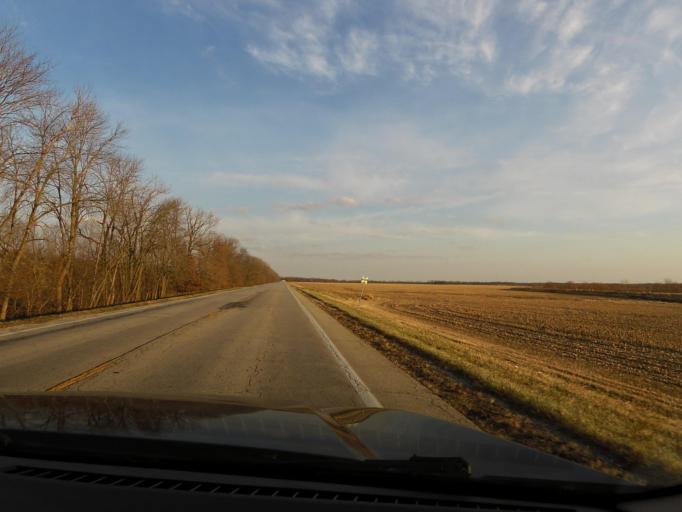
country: US
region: Illinois
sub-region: Fayette County
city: Vandalia
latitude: 38.9389
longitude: -89.0852
